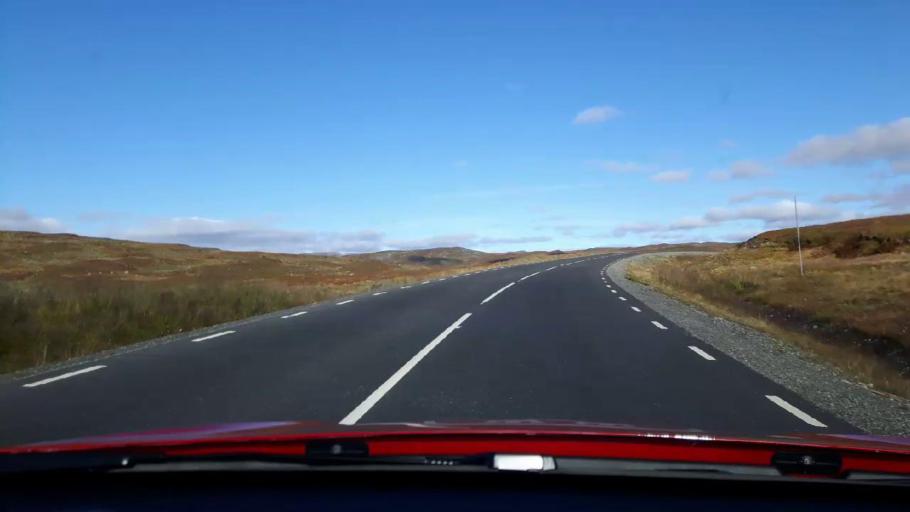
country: NO
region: Nordland
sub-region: Hattfjelldal
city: Hattfjelldal
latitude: 65.0386
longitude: 14.3270
